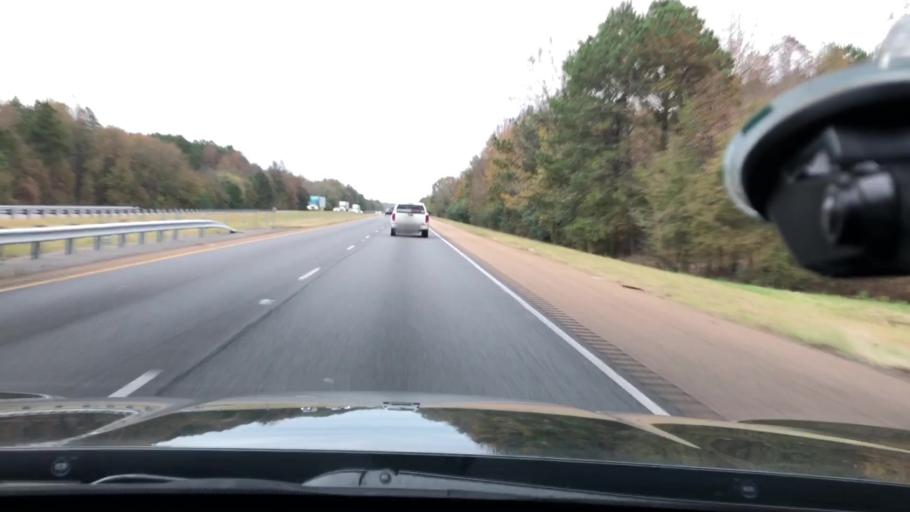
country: US
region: Arkansas
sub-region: Nevada County
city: Prescott
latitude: 33.8806
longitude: -93.3279
